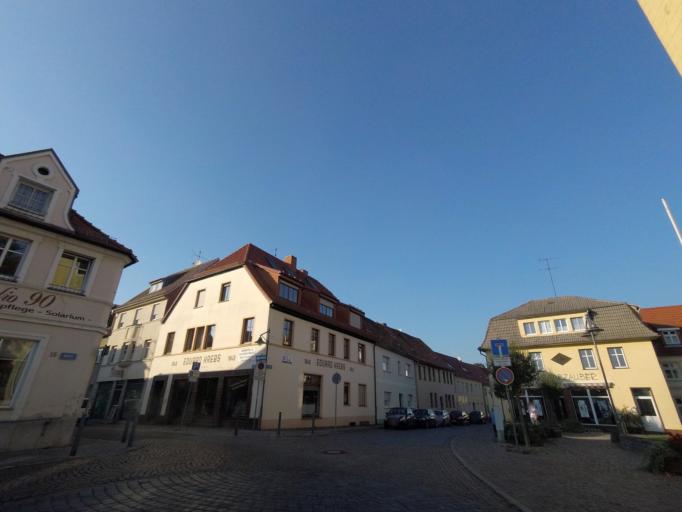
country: DE
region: Saxony-Anhalt
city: Jessen
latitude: 51.7861
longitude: 12.9572
